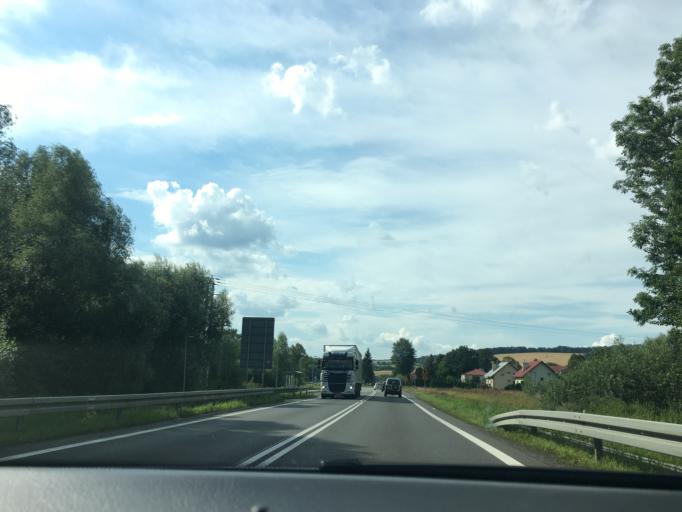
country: PL
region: Subcarpathian Voivodeship
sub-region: Powiat strzyzowski
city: Babica
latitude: 49.9260
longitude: 21.8765
